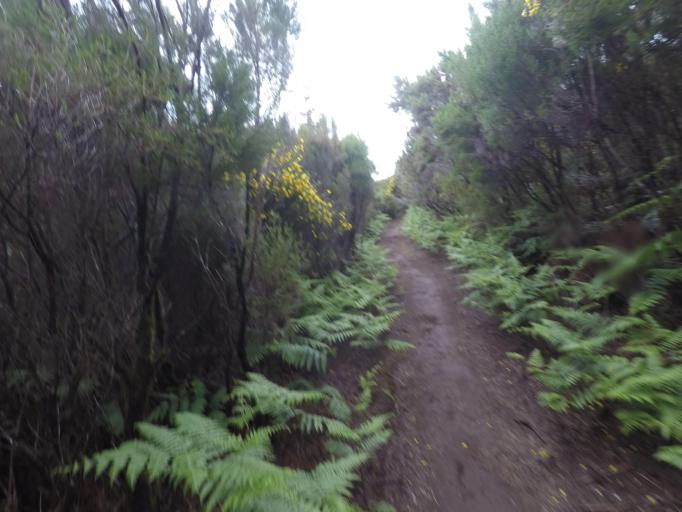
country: PT
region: Madeira
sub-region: Calheta
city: Arco da Calheta
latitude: 32.7777
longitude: -17.1327
